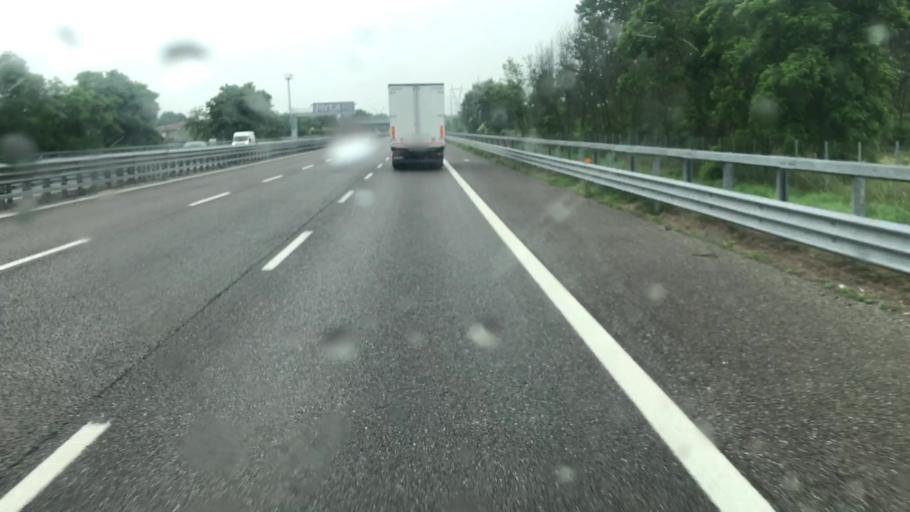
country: IT
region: Lombardy
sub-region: Provincia di Pavia
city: Trivolzio
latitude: 45.2548
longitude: 9.0479
